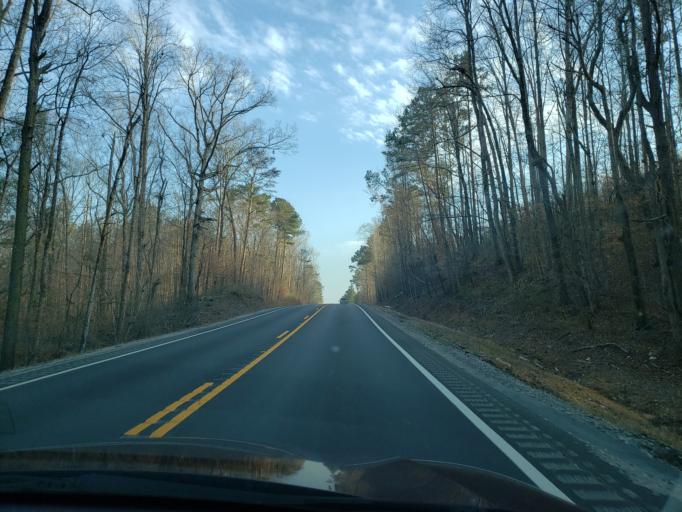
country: US
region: Alabama
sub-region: Hale County
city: Greensboro
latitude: 32.8415
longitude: -87.6088
